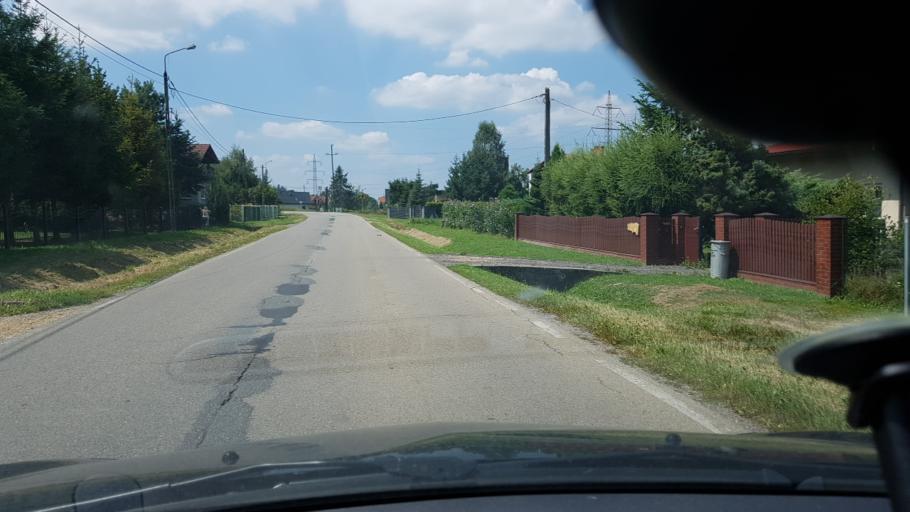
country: PL
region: Lesser Poland Voivodeship
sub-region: Powiat oswiecimski
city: Babice
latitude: 50.0556
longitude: 19.1932
